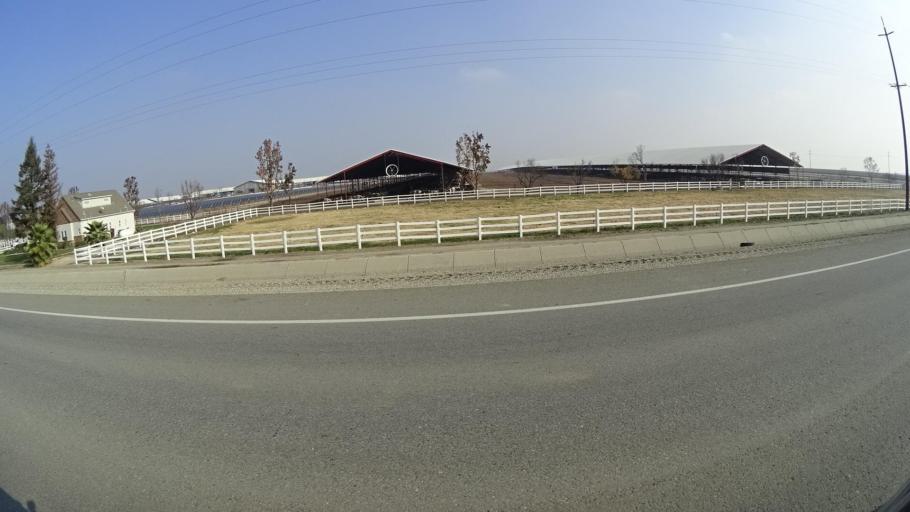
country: US
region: California
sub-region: Kern County
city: Greenfield
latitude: 35.1685
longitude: -119.1096
